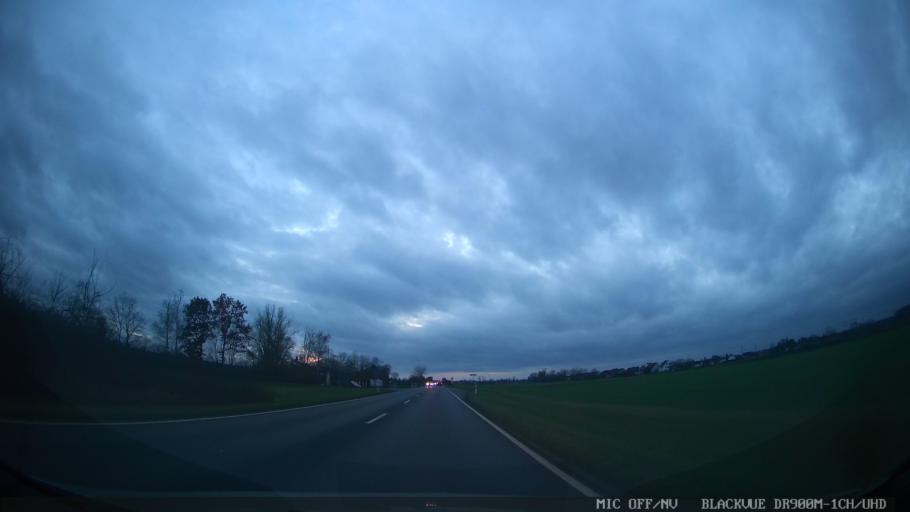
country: DE
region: Hesse
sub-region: Regierungsbezirk Darmstadt
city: Babenhausen
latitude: 49.9491
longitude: 8.9443
